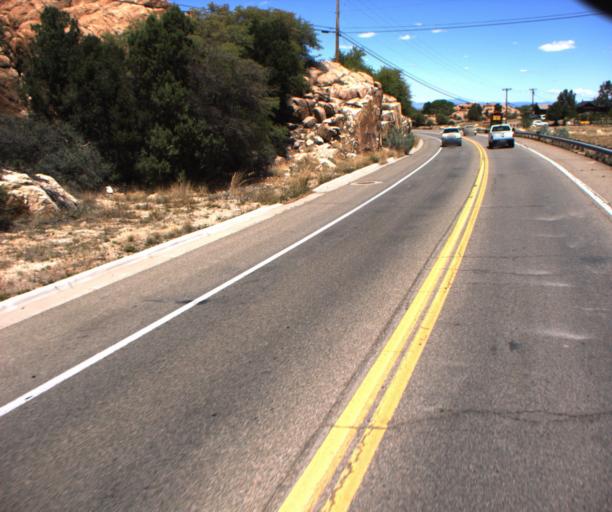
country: US
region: Arizona
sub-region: Yavapai County
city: Prescott
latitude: 34.6108
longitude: -112.4193
